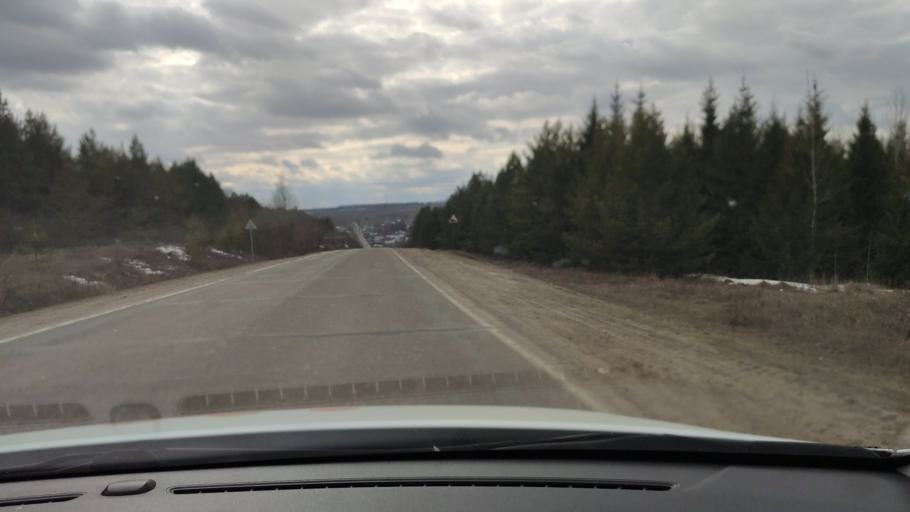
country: RU
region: Tatarstan
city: Vysokaya Gora
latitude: 56.1279
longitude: 49.2061
